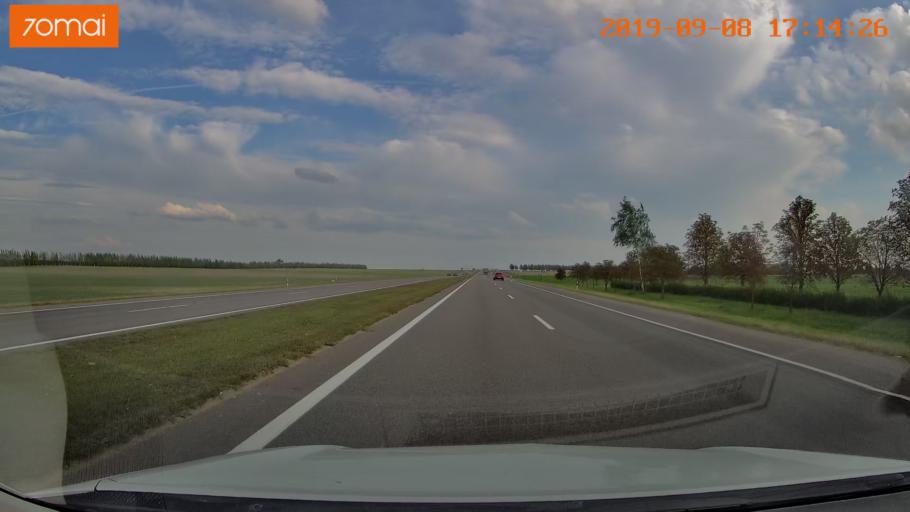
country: BY
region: Grodnenskaya
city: Skidal'
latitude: 53.6154
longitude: 24.0740
